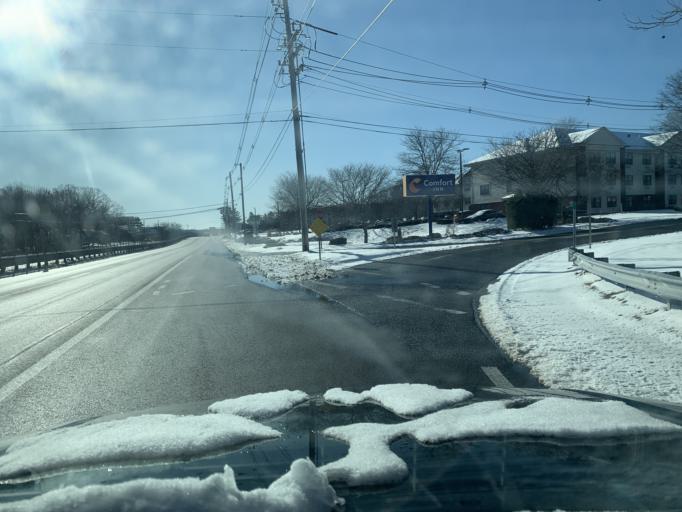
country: US
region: Massachusetts
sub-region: Essex County
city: Danvers
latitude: 42.5678
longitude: -70.9745
